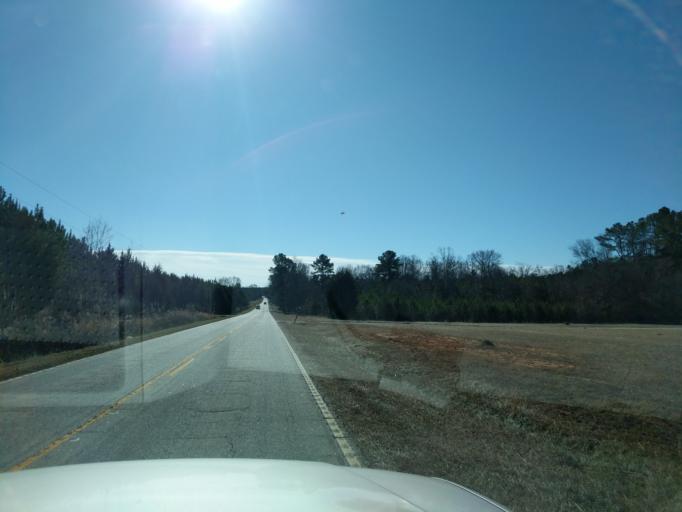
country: US
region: South Carolina
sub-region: Laurens County
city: Joanna
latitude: 34.3456
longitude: -81.8556
